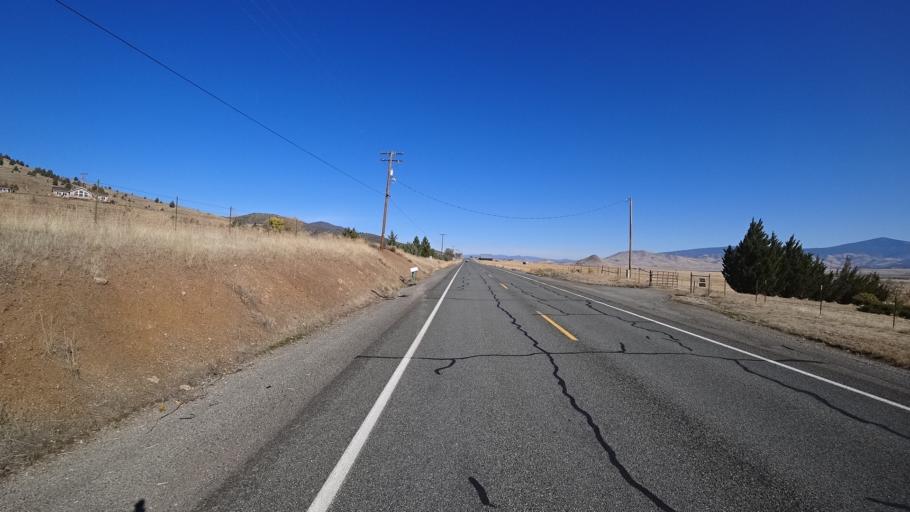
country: US
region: California
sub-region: Siskiyou County
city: Montague
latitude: 41.7883
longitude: -122.5162
